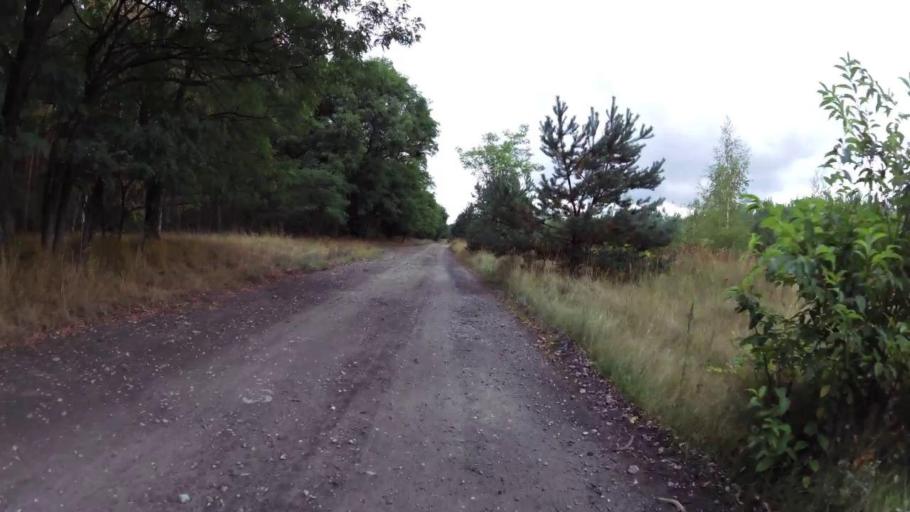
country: PL
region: West Pomeranian Voivodeship
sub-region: Powiat mysliborski
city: Debno
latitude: 52.8608
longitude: 14.7180
